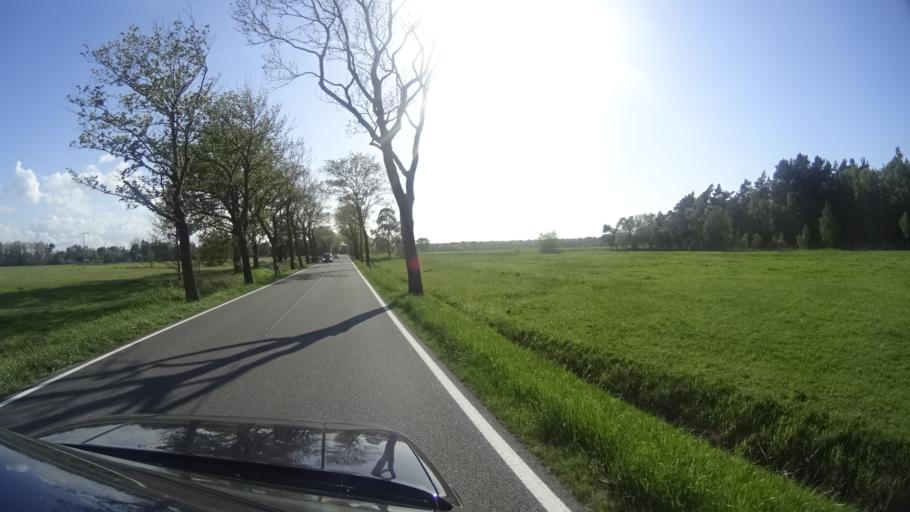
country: DE
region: Mecklenburg-Vorpommern
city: Born
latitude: 54.3950
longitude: 12.5556
